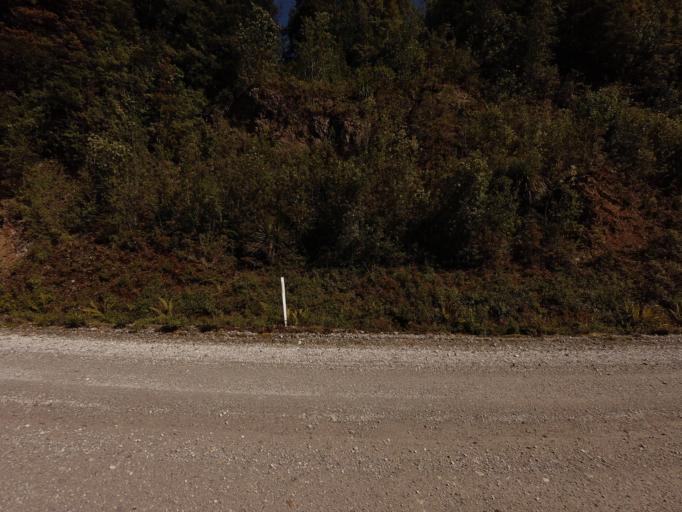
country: AU
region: Tasmania
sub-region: Huon Valley
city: Geeveston
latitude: -42.8405
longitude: 146.3759
